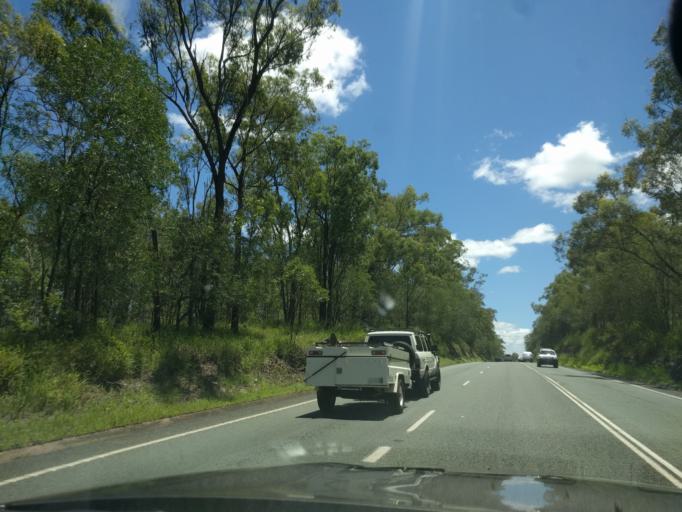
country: AU
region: Queensland
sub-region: Logan
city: Cedar Vale
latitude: -27.8417
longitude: 153.0235
